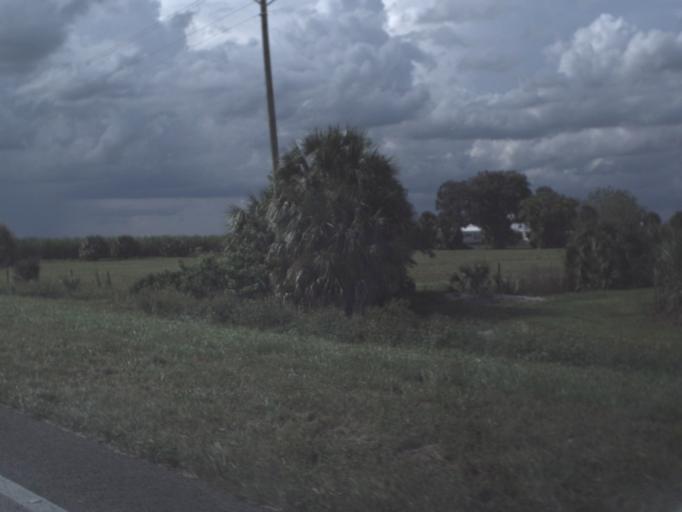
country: US
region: Florida
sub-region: Hendry County
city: Harlem
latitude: 26.7543
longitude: -80.9981
